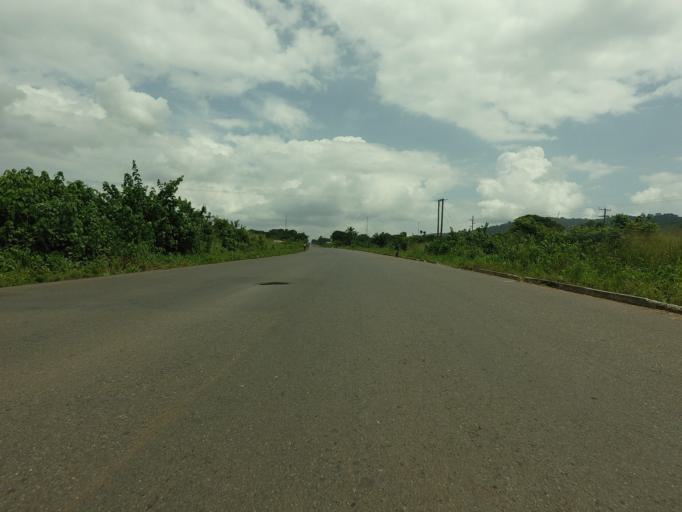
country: GH
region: Volta
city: Ho
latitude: 6.5375
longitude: 0.2330
